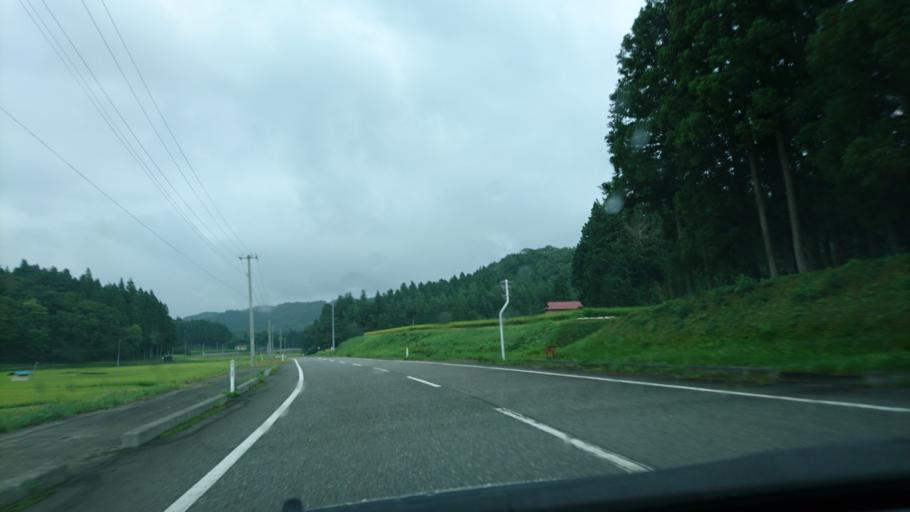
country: JP
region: Iwate
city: Ichinoseki
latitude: 38.8845
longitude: 140.9663
